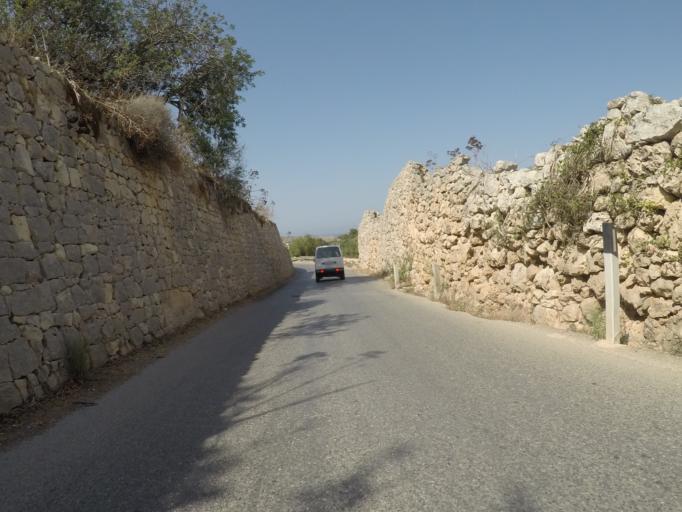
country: MT
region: L-Imgarr
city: Imgarr
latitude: 35.9359
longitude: 14.3801
